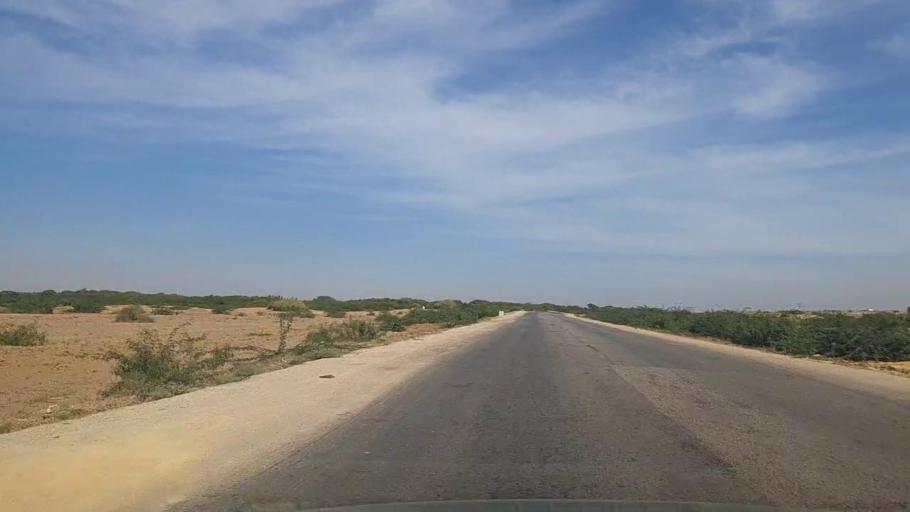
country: PK
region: Sindh
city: Daro Mehar
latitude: 24.9932
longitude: 68.1448
